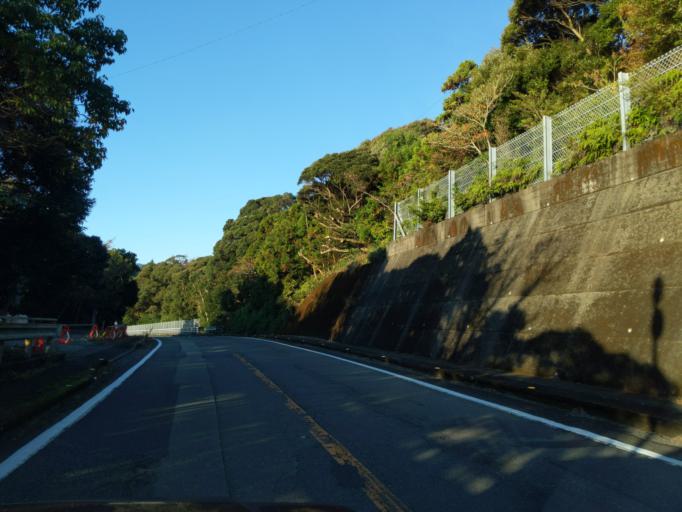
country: JP
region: Kochi
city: Muroto-misakicho
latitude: 33.5457
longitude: 134.3004
